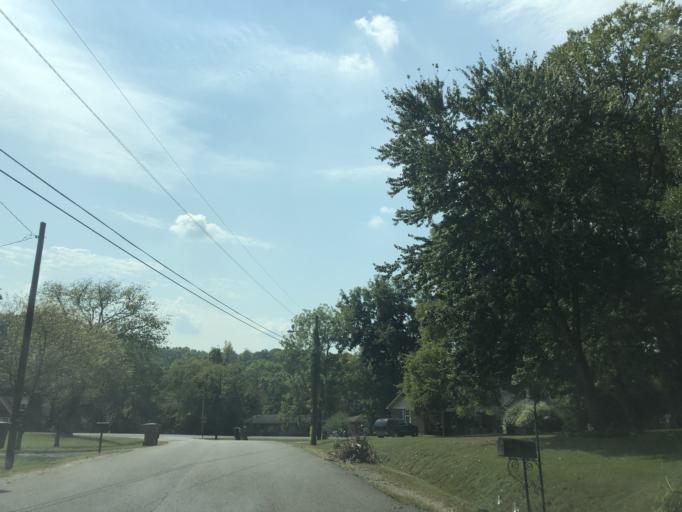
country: US
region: Tennessee
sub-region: Davidson County
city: Lakewood
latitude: 36.1554
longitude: -86.6464
